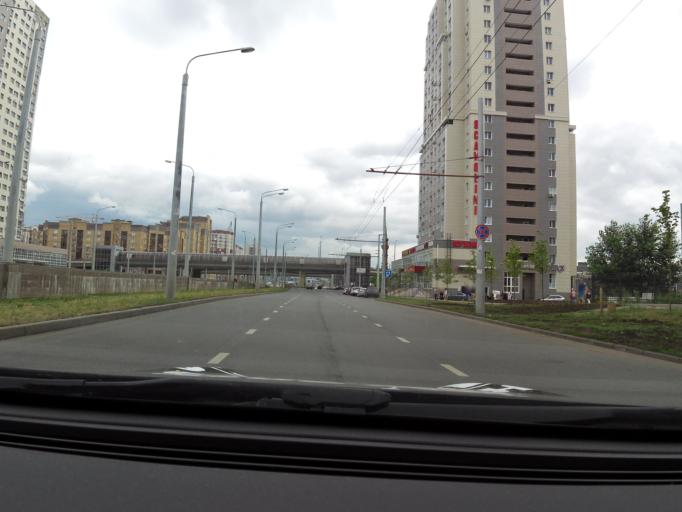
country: RU
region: Tatarstan
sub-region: Gorod Kazan'
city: Kazan
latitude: 55.8211
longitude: 49.1333
